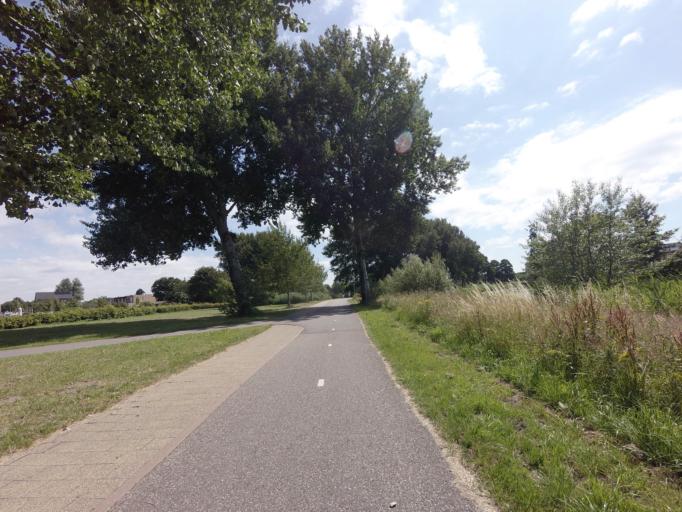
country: NL
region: Flevoland
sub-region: Gemeente Almere
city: Almere Stad
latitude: 52.3459
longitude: 5.2059
